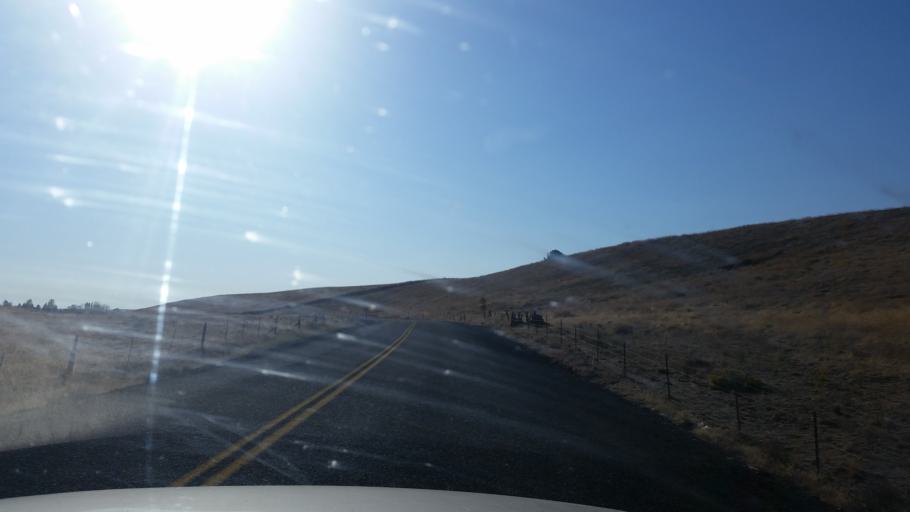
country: US
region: Washington
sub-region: Spokane County
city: Cheney
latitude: 47.3598
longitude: -117.7000
